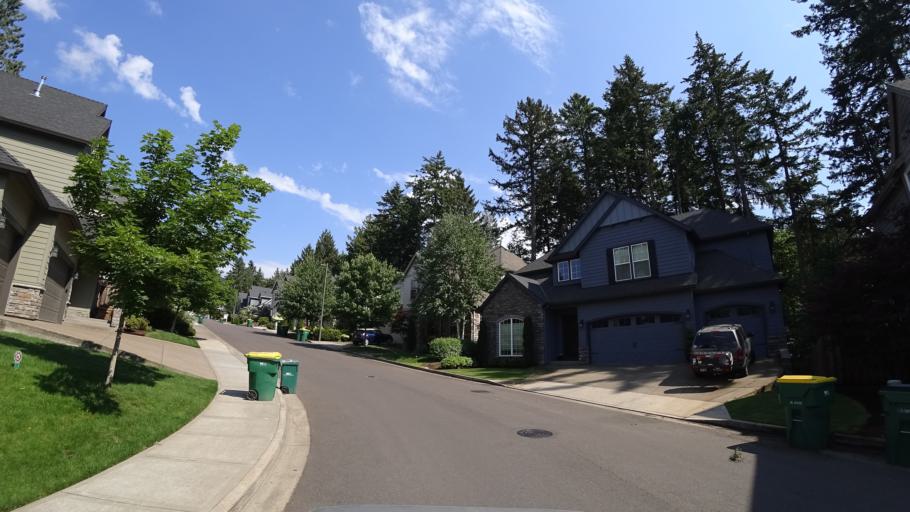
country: US
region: Oregon
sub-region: Washington County
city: Metzger
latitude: 45.4494
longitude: -122.7513
